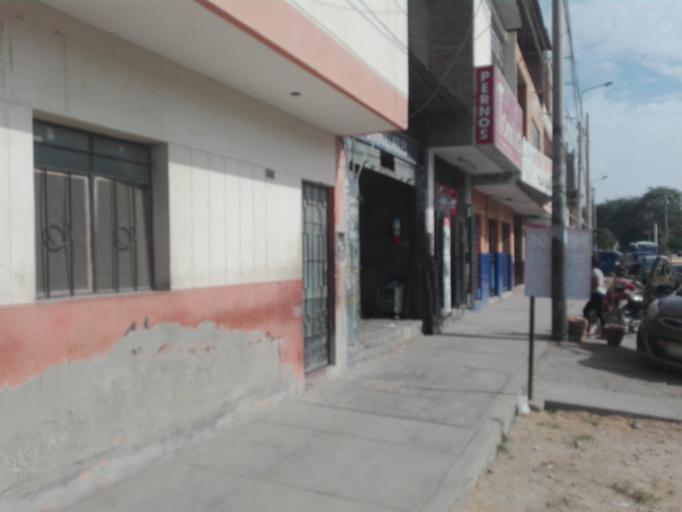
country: PE
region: Piura
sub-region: Provincia de Piura
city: Piura
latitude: -5.1872
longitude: -80.6323
